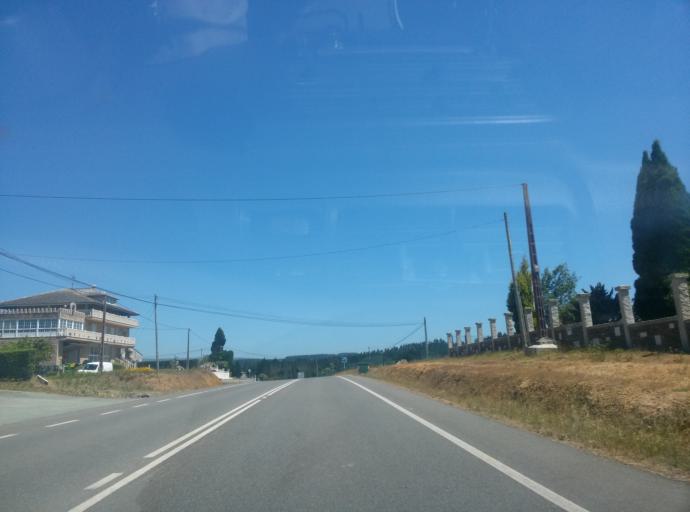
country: ES
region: Galicia
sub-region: Provincia de Lugo
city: Castro de Rei
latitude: 43.2357
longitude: -7.3999
